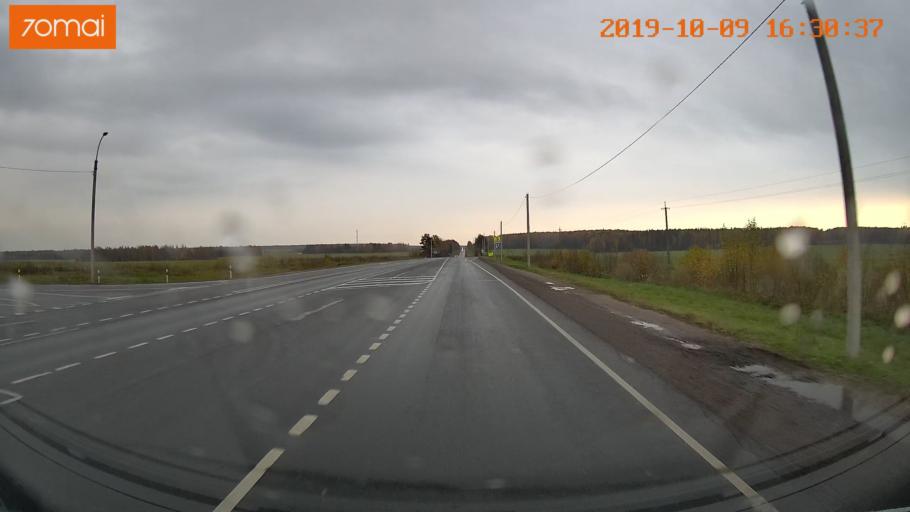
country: RU
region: Kostroma
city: Oktyabr'skiy
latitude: 57.6171
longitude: 40.9420
